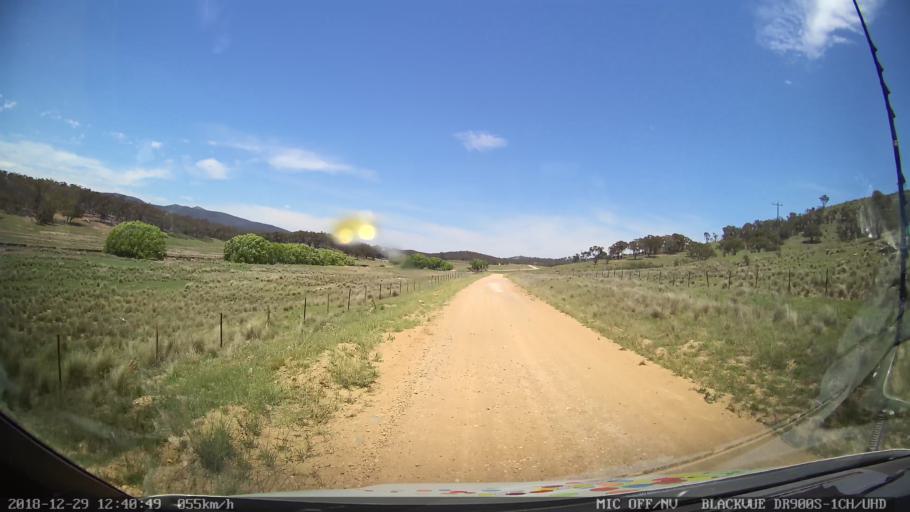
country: AU
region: Australian Capital Territory
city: Macarthur
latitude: -35.6042
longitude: 149.2236
